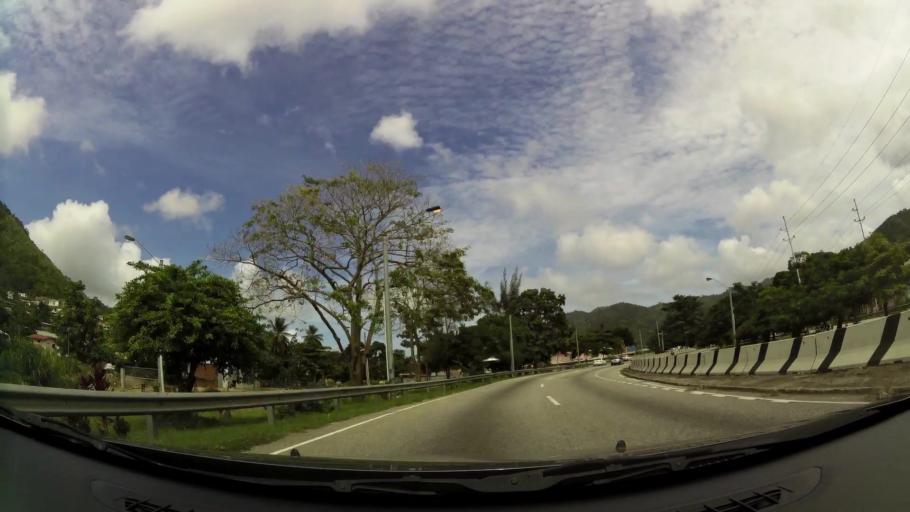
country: TT
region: Diego Martin
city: Petit Valley
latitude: 10.6988
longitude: -61.5545
